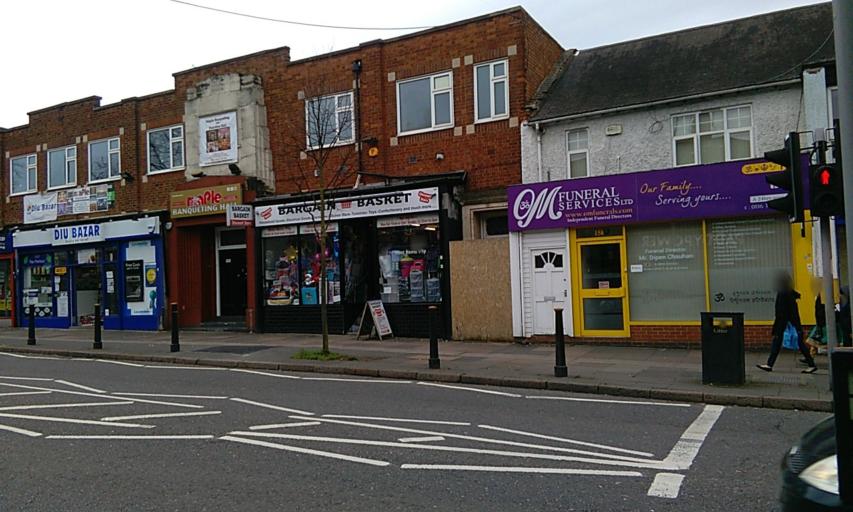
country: GB
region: England
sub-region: City of Leicester
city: Leicester
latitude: 52.6563
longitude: -1.1175
